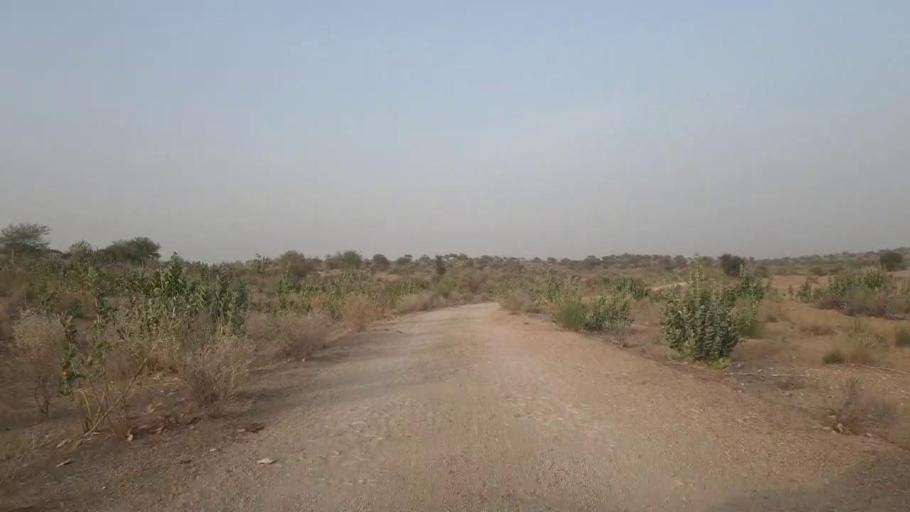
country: PK
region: Sindh
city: Chor
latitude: 25.5176
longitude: 69.9481
